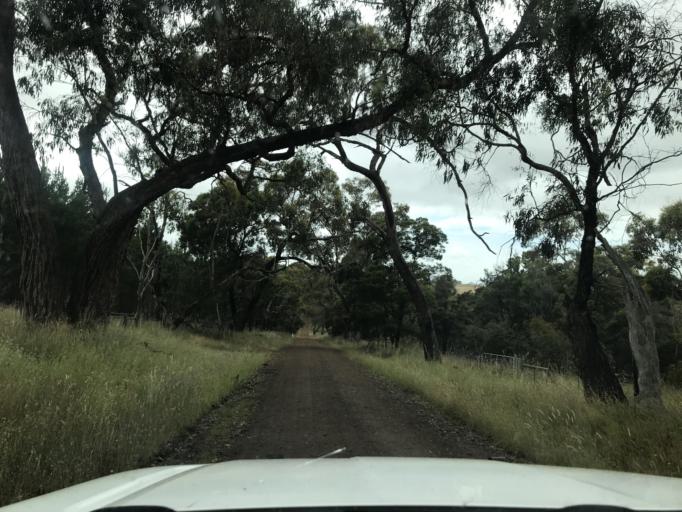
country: AU
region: South Australia
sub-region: Wattle Range
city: Penola
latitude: -37.2345
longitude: 141.4323
